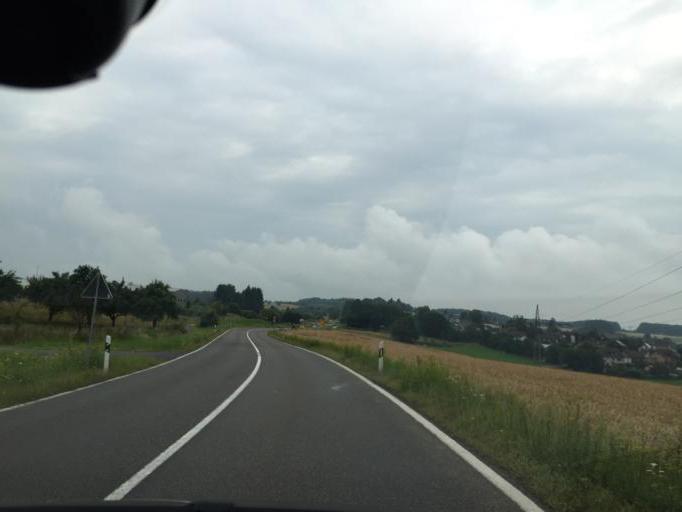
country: DE
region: Rheinland-Pfalz
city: Bonefeld
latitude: 50.5185
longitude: 7.4857
